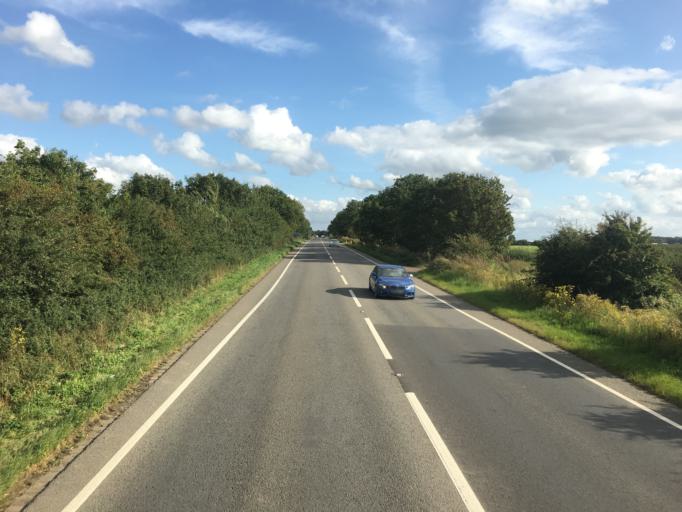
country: GB
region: England
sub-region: Leicestershire
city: Lutterworth
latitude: 52.4288
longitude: -1.2310
